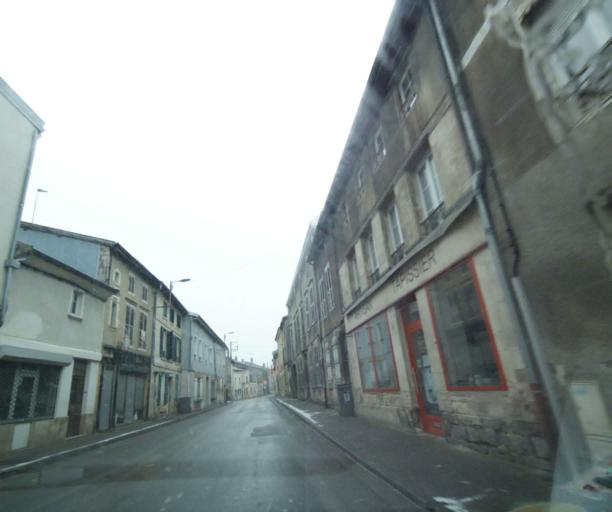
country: FR
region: Champagne-Ardenne
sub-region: Departement de la Haute-Marne
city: Wassy
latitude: 48.4974
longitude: 4.9493
